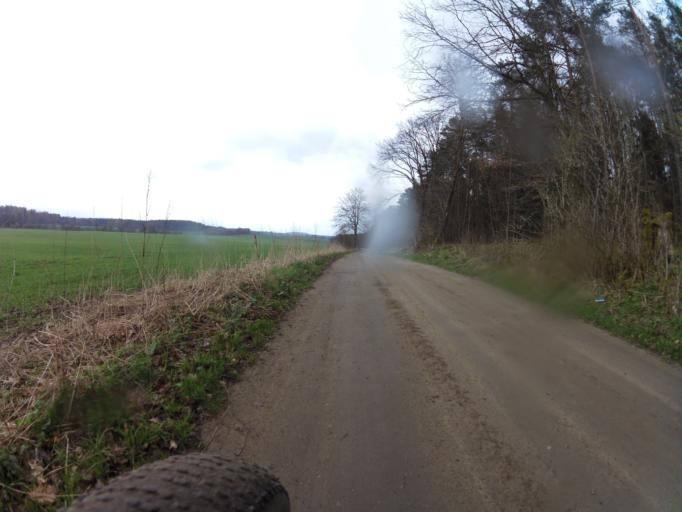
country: PL
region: West Pomeranian Voivodeship
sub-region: Powiat koszalinski
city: Polanow
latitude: 54.2126
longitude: 16.7424
